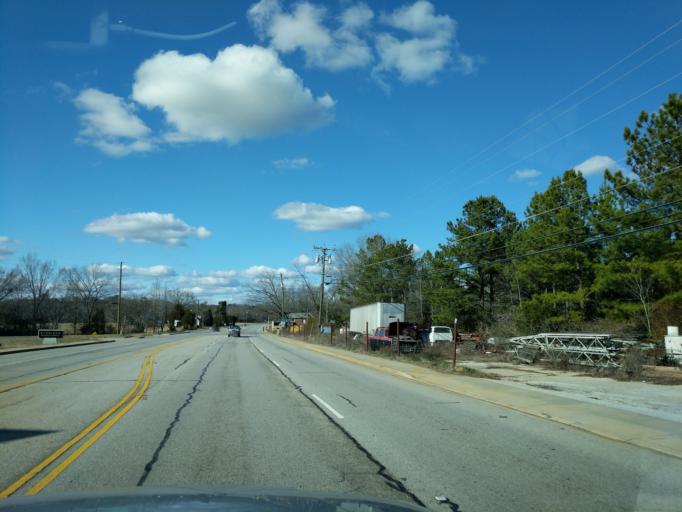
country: US
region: South Carolina
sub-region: Greenwood County
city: Greenwood
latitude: 34.1283
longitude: -82.1236
